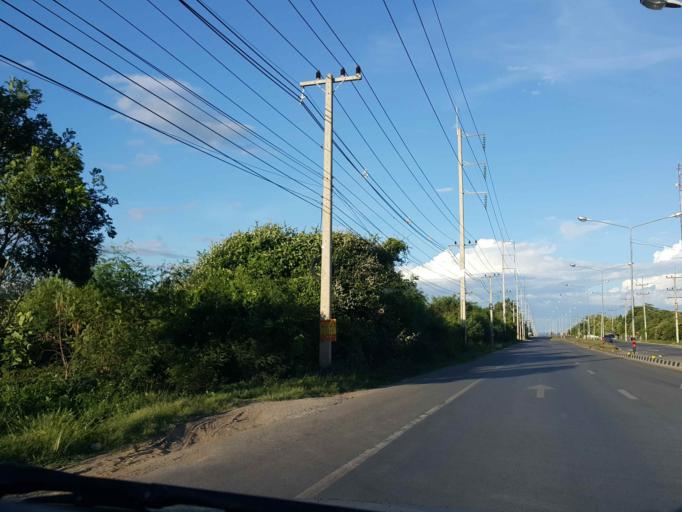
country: TH
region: Lamphun
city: Wiang Nong Long
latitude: 18.4519
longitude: 98.7198
